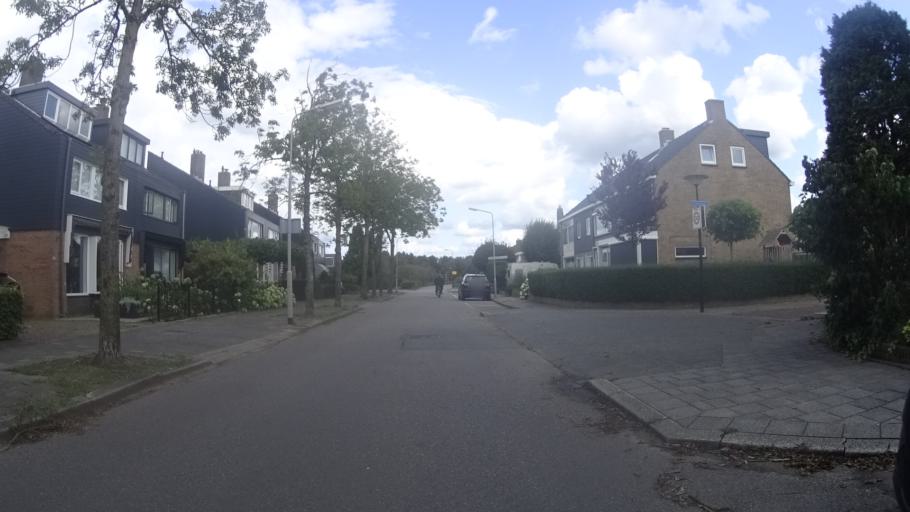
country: NL
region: North Holland
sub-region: Gemeente Beverwijk
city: Beverwijk
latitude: 52.4921
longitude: 4.6458
